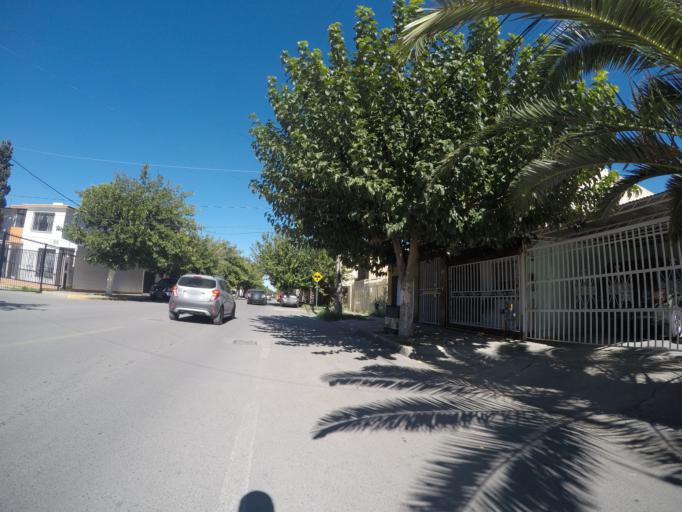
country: MX
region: Chihuahua
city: Ciudad Juarez
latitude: 31.7152
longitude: -106.4200
